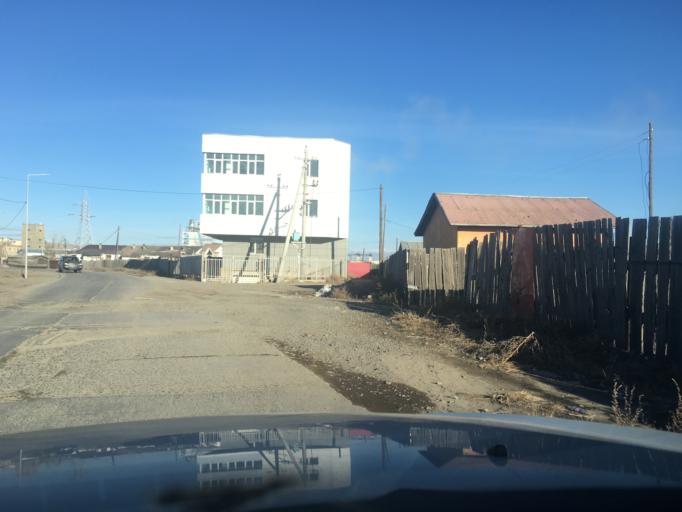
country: MN
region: Ulaanbaatar
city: Ulaanbaatar
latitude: 47.9028
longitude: 106.8000
